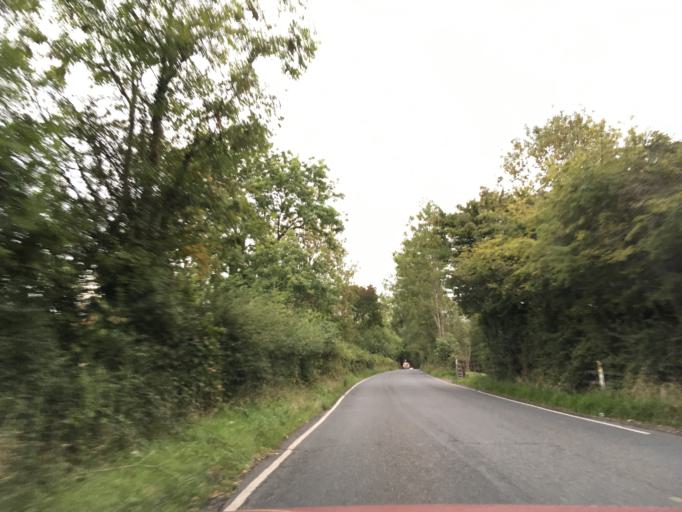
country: GB
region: Wales
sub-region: Newport
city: Langstone
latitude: 51.6108
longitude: -2.9115
